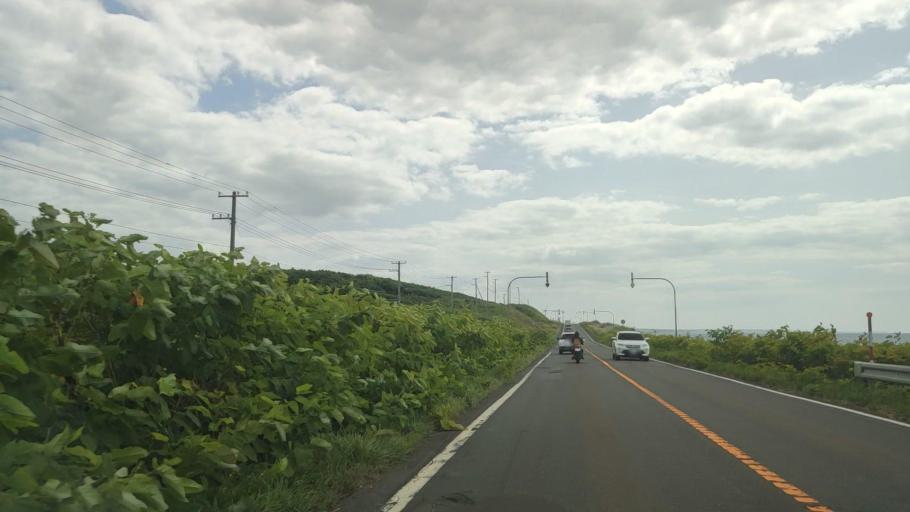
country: JP
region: Hokkaido
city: Rumoi
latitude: 44.5065
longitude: 141.7648
